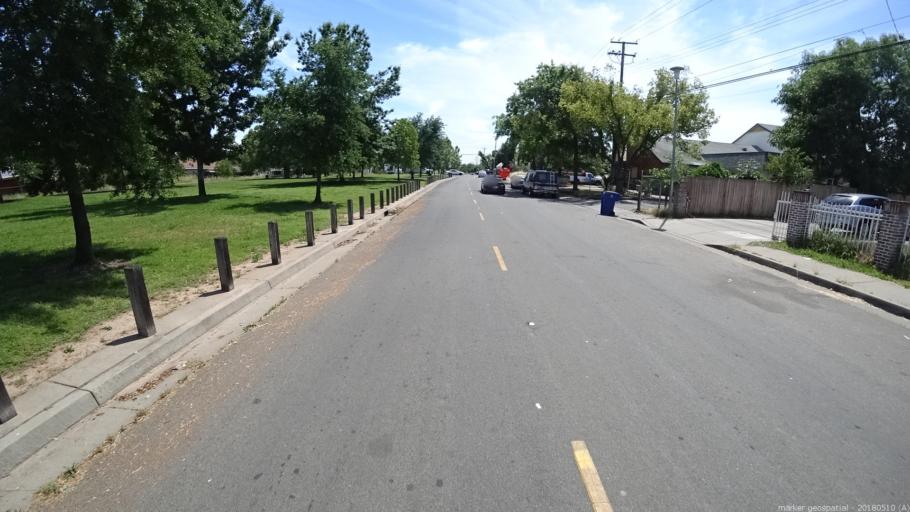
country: US
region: California
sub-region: Sacramento County
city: Rio Linda
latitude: 38.6297
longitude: -121.4480
